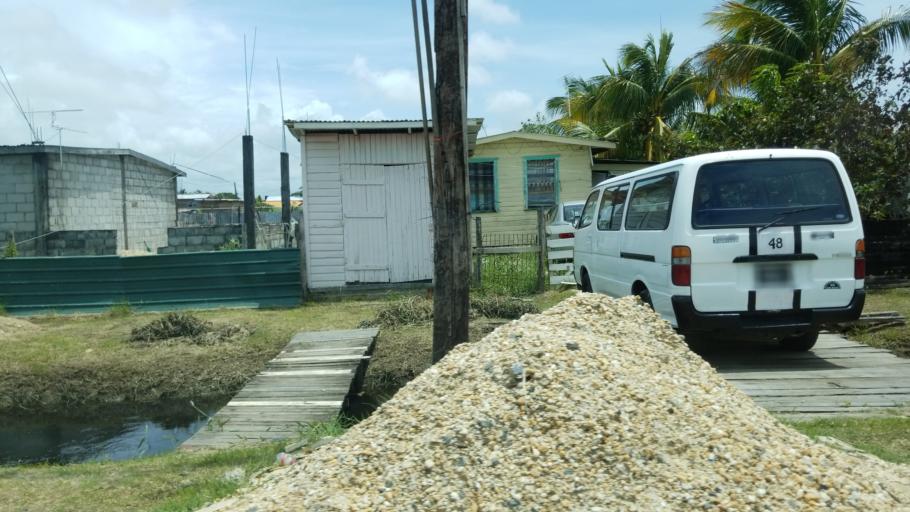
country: GY
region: Demerara-Mahaica
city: Georgetown
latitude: 6.7963
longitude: -58.1192
